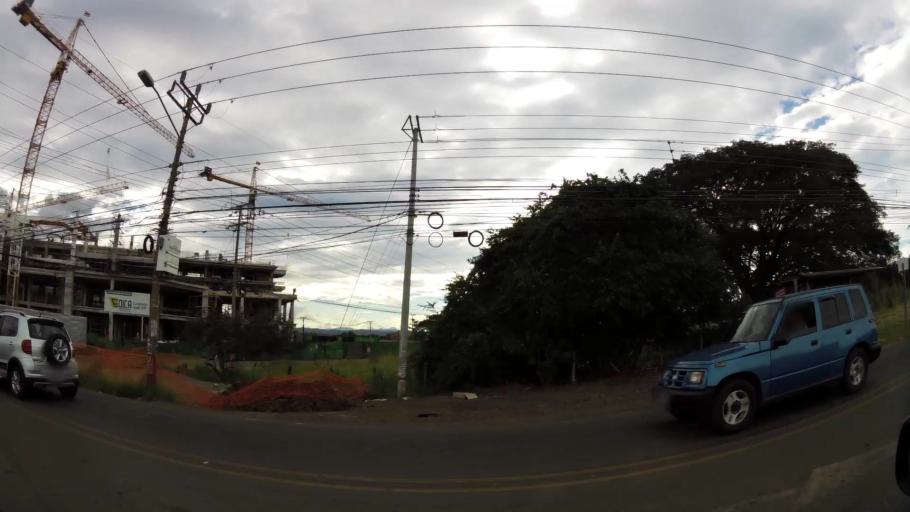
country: CR
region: Heredia
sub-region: Canton de Belen
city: San Antonio
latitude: 9.9584
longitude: -84.1963
